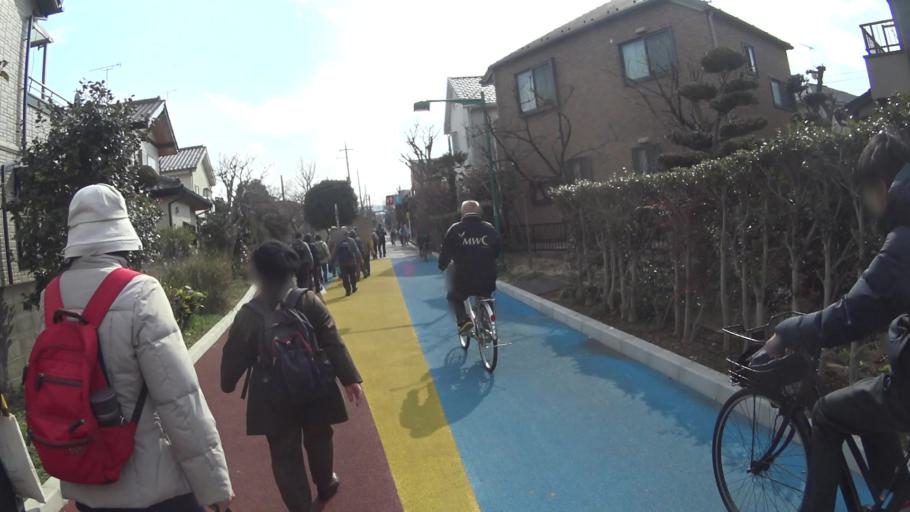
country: JP
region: Tokyo
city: Kokubunji
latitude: 35.6651
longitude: 139.4737
